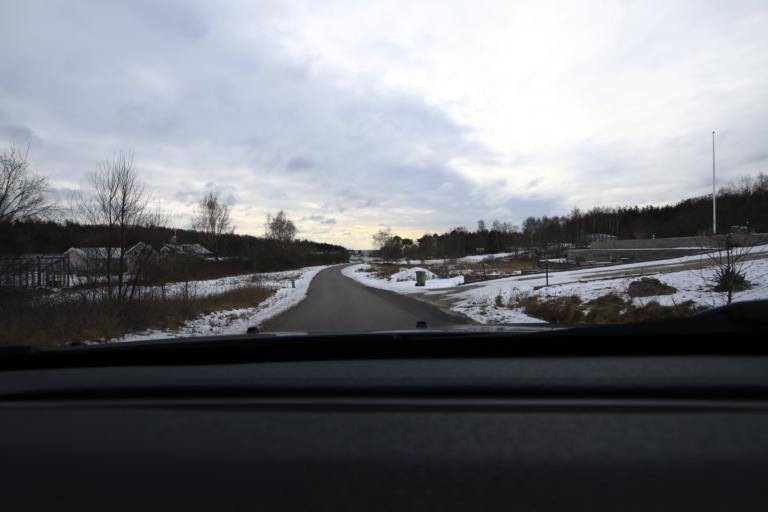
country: SE
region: Halland
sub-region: Kungsbacka Kommun
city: Frillesas
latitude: 57.2209
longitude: 12.1592
